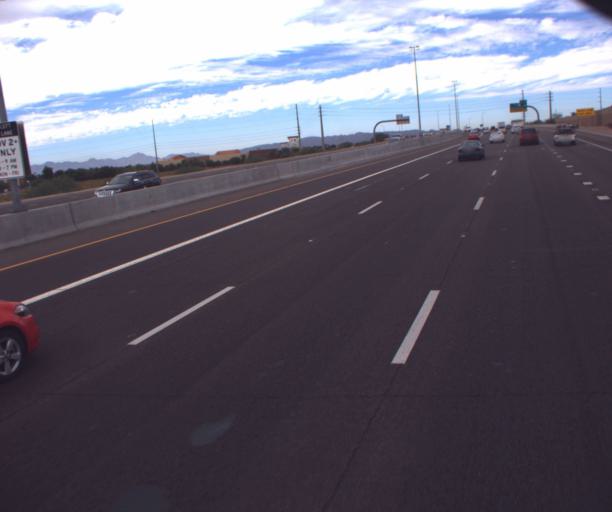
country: US
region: Arizona
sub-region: Maricopa County
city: Chandler
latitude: 33.2849
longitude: -111.8321
